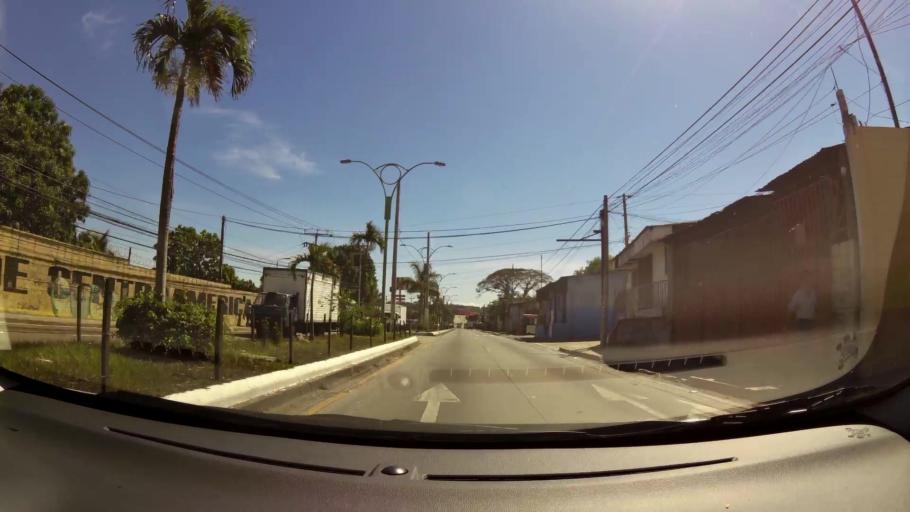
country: SV
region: San Salvador
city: Apopa
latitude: 13.7932
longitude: -89.1765
